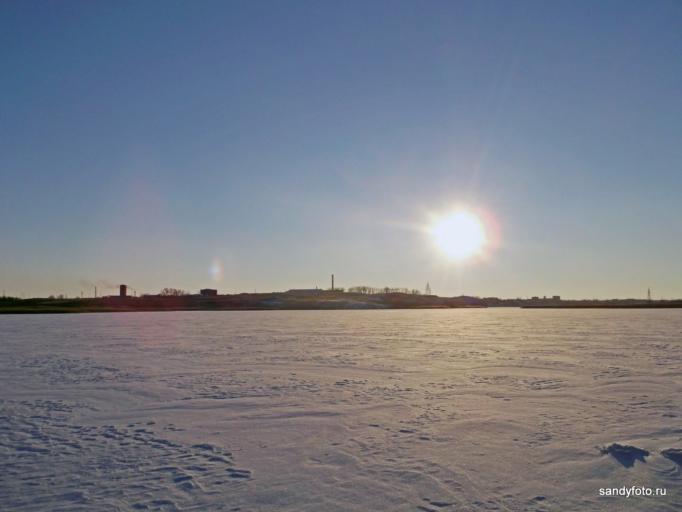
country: RU
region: Chelyabinsk
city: Troitsk
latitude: 54.0875
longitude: 61.5905
